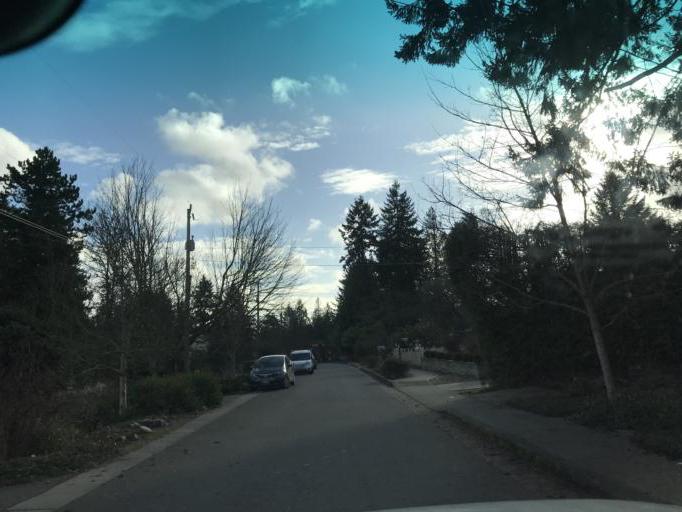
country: US
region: Washington
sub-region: King County
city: Lake Forest Park
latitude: 47.7135
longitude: -122.3072
